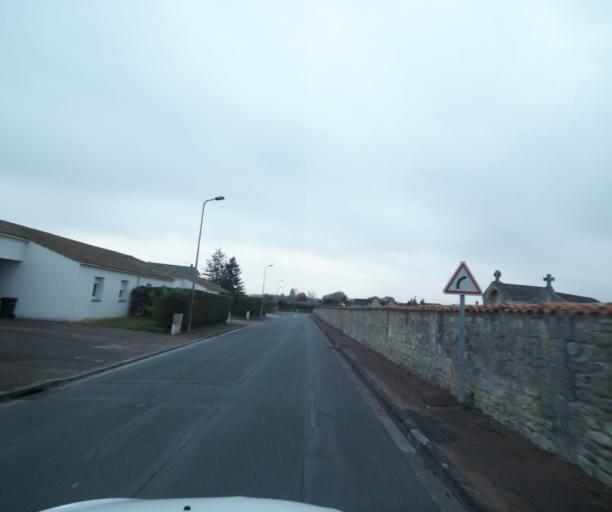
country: FR
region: Poitou-Charentes
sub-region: Departement de la Charente-Maritime
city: Saintes
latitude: 45.7407
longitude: -0.6166
